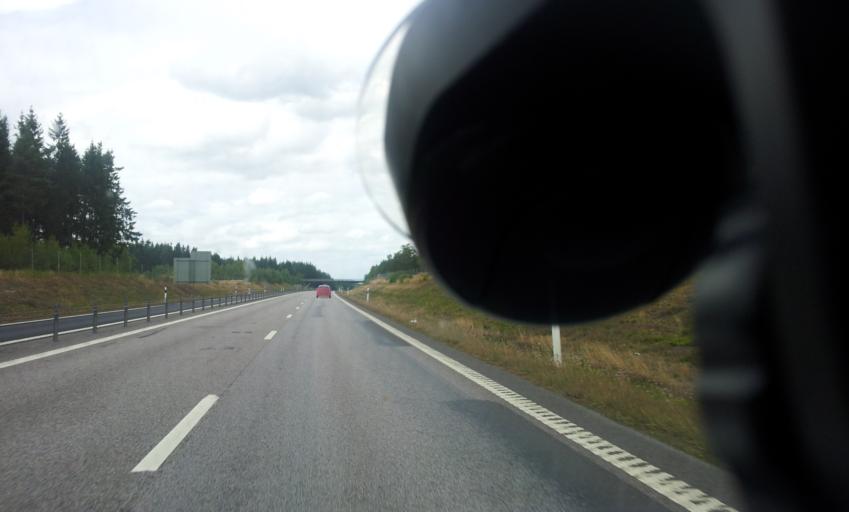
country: SE
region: Kalmar
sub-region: Torsas Kommun
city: Torsas
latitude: 56.4591
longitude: 16.0785
